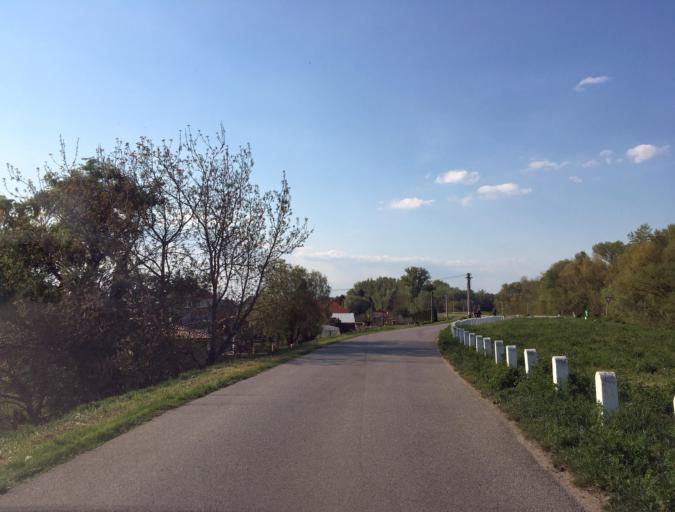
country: SK
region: Nitriansky
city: Kolarovo
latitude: 47.9138
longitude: 18.0080
